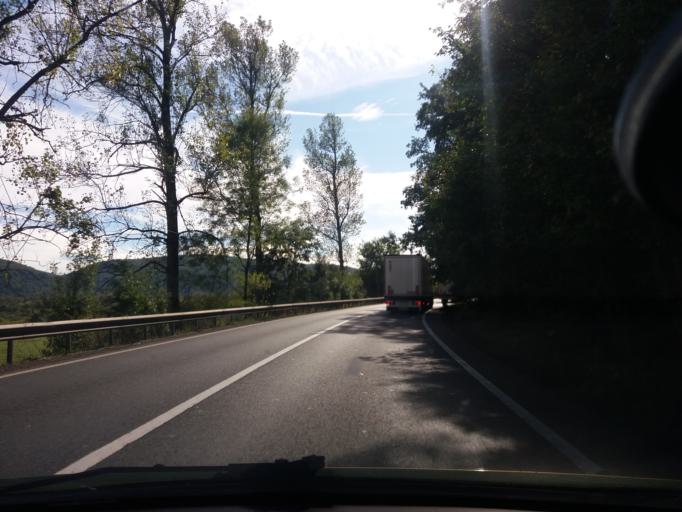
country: RO
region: Arad
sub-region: Comuna Petris
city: Petris
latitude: 46.0089
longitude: 22.3444
